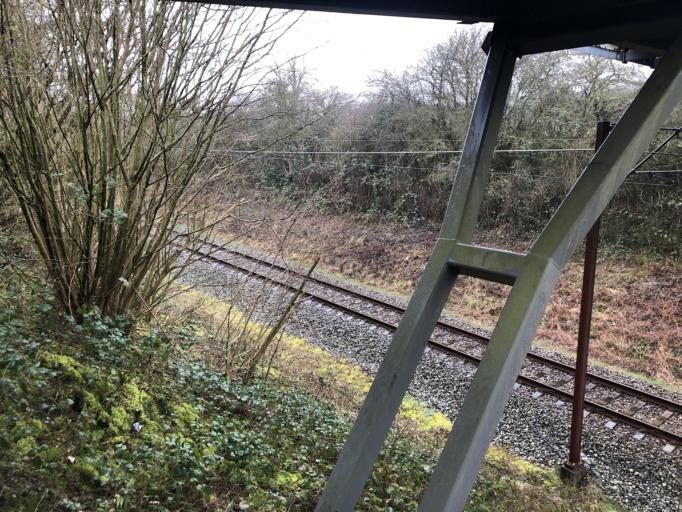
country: DK
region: South Denmark
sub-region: Sonderborg Kommune
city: Grasten
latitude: 54.9097
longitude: 9.5753
